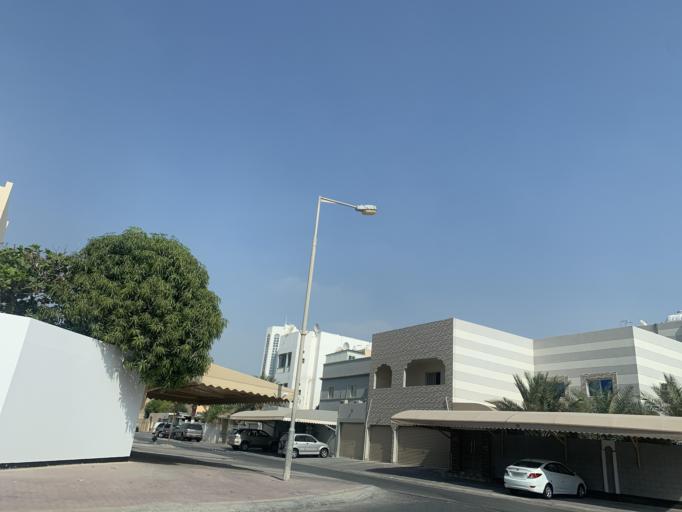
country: BH
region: Central Governorate
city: Madinat Hamad
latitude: 26.1251
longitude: 50.4906
